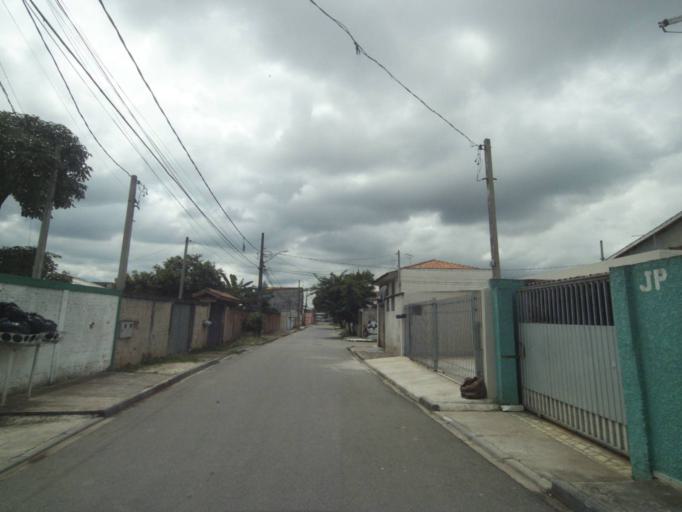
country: BR
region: Parana
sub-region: Pinhais
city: Pinhais
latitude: -25.4589
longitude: -49.1980
